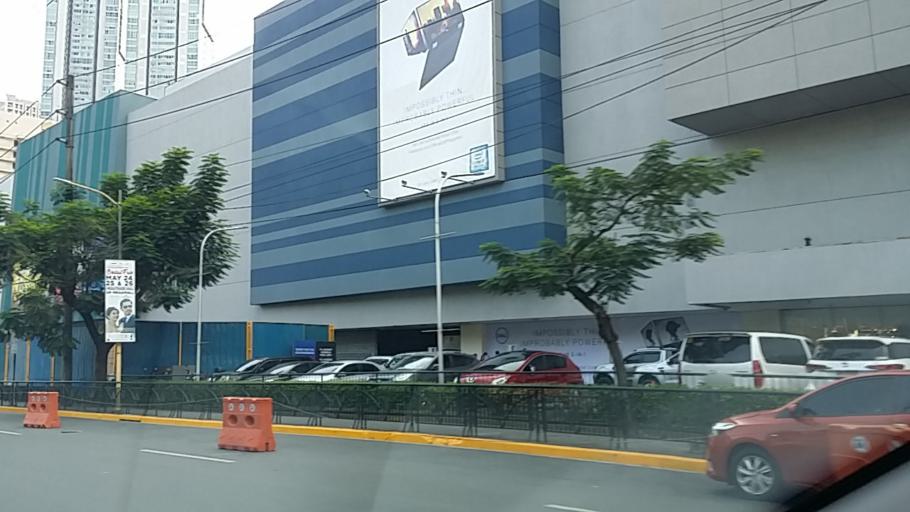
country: PH
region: Metro Manila
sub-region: Pasig
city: Pasig City
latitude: 14.5835
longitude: 121.0579
